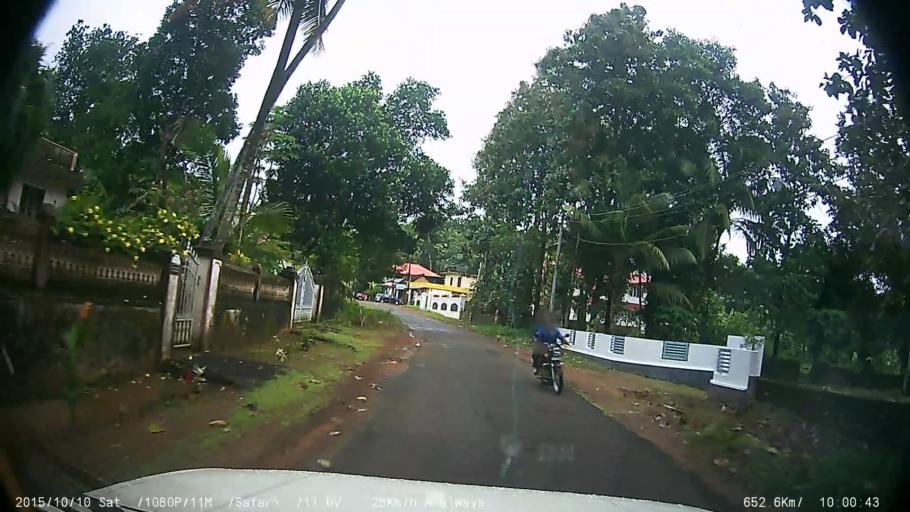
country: IN
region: Kerala
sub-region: Kottayam
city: Kottayam
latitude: 9.6399
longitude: 76.5360
